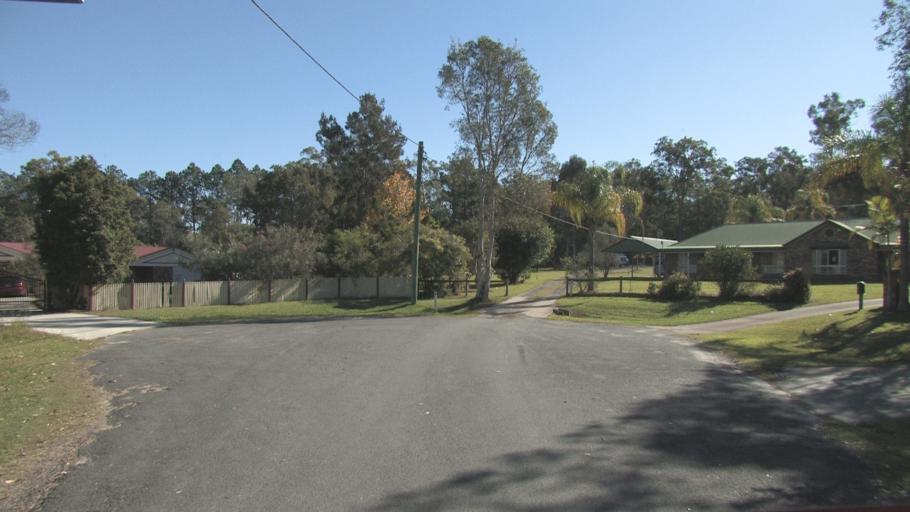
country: AU
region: Queensland
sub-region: Logan
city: Logan Reserve
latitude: -27.7214
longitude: 153.0682
